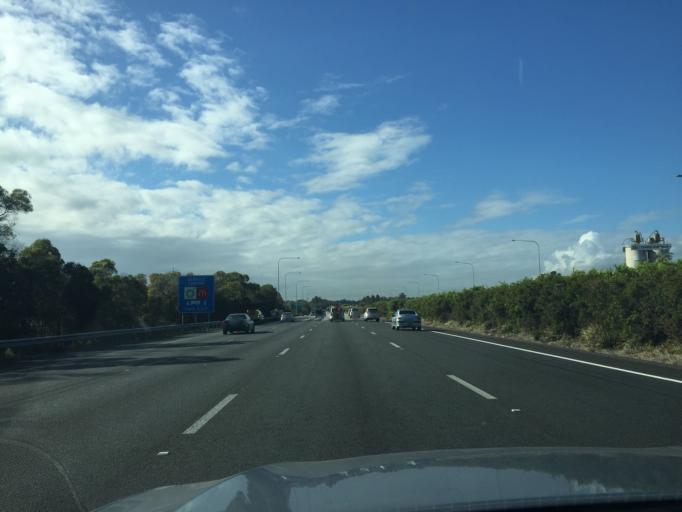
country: AU
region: Queensland
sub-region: Gold Coast
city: Yatala
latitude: -27.7292
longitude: 153.2236
